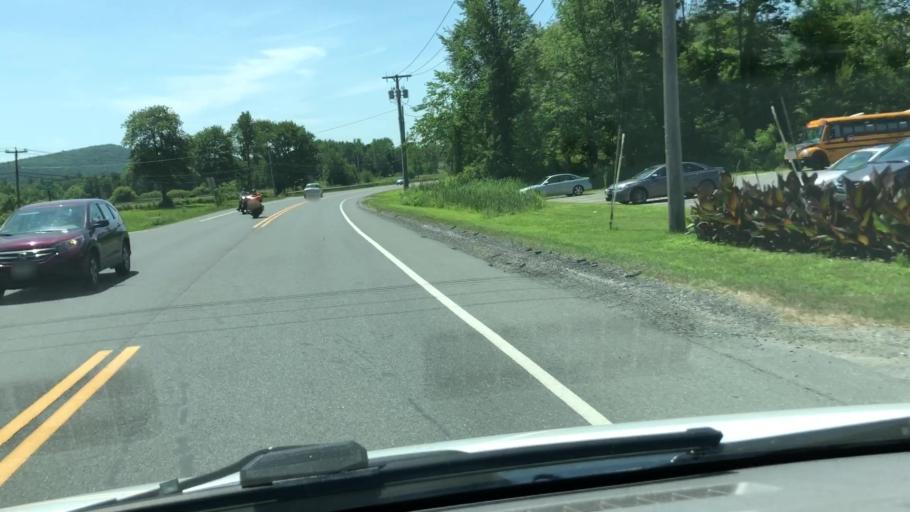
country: US
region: Massachusetts
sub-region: Franklin County
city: South Deerfield
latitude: 42.5096
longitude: -72.6052
